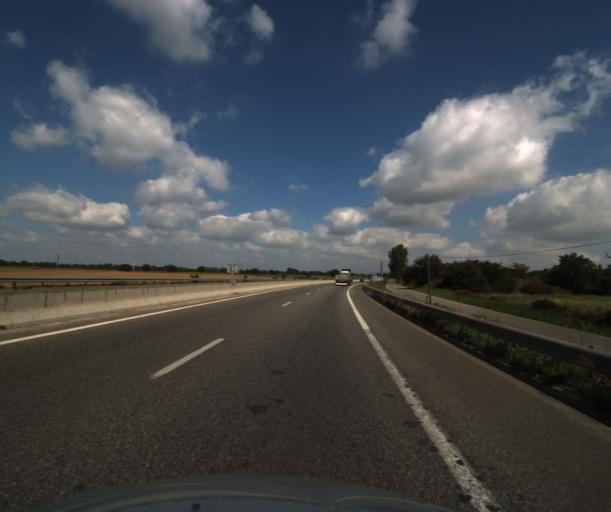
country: FR
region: Midi-Pyrenees
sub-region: Departement de la Haute-Garonne
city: Pinsaguel
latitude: 43.4977
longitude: 1.3886
